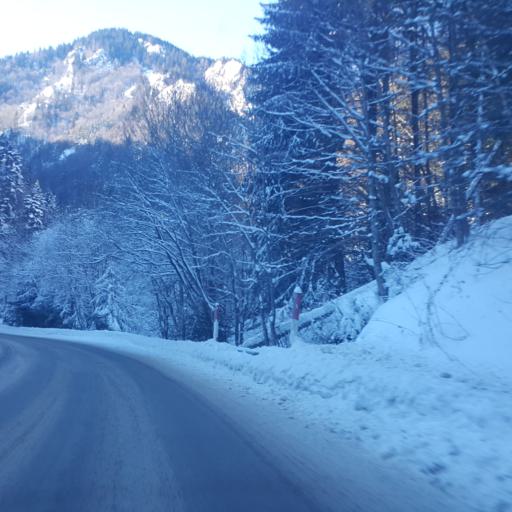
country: XK
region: Mitrovica
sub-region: Komuna e Leposaviqit
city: Leposaviq
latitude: 43.3059
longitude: 20.8601
